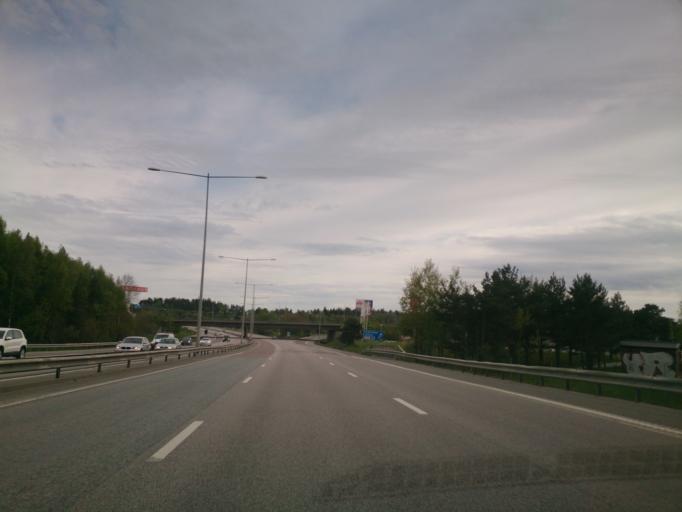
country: SE
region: Stockholm
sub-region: Haninge Kommun
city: Handen
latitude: 59.2030
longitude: 18.1310
